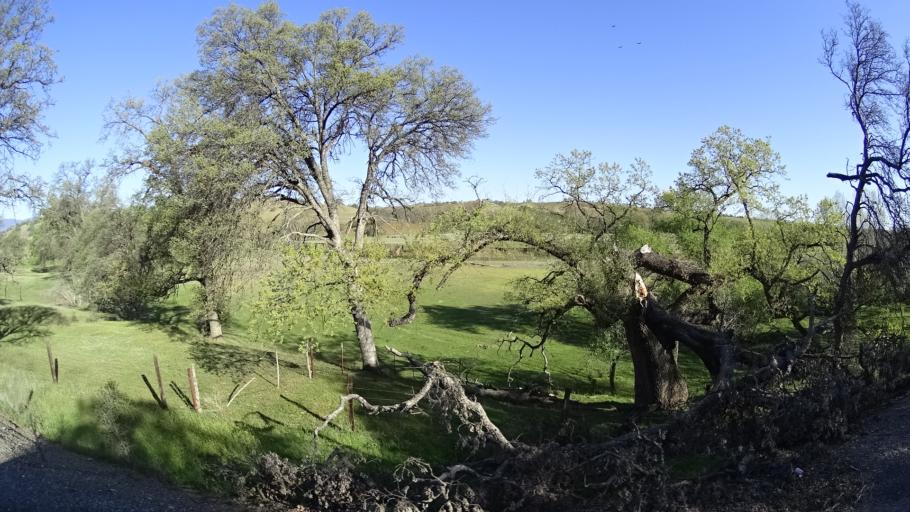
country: US
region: California
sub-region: Tehama County
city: Rancho Tehama Reserve
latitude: 39.7897
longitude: -122.4560
